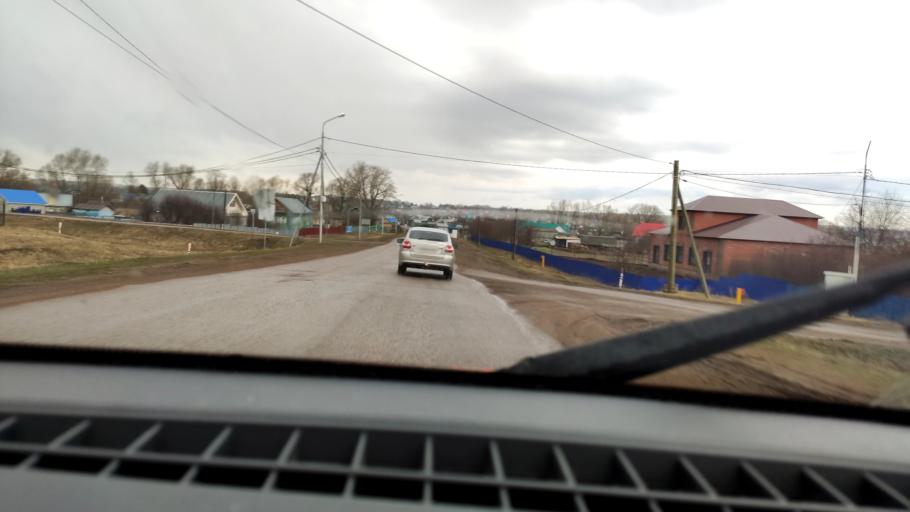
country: RU
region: Bashkortostan
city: Chekmagush
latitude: 55.1328
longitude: 54.6754
